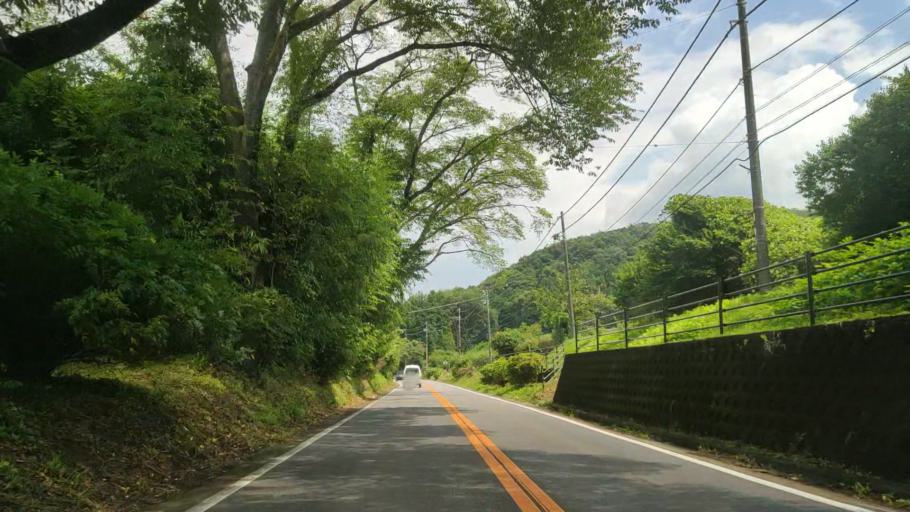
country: JP
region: Tochigi
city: Utsunomiya-shi
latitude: 36.6680
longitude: 139.8199
